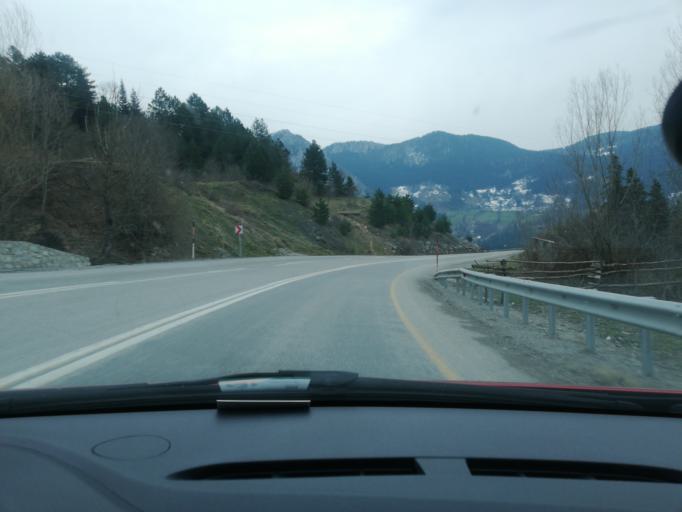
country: TR
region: Kastamonu
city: Kure
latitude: 41.8490
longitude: 33.7203
